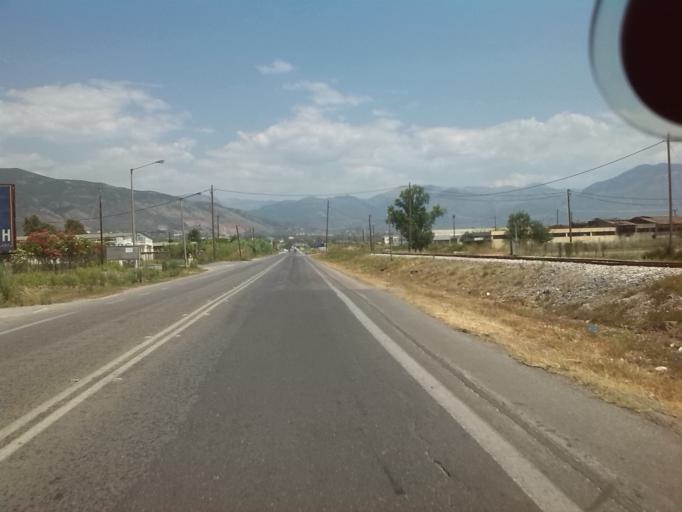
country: GR
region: Peloponnese
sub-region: Nomos Messinias
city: Sperkhoyia
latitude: 37.0559
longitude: 22.0477
